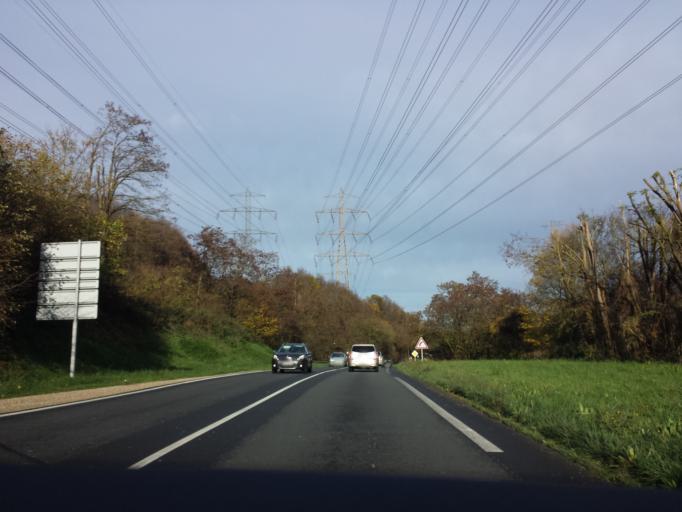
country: FR
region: Ile-de-France
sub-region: Departement de l'Essonne
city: Igny
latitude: 48.7405
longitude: 2.2249
